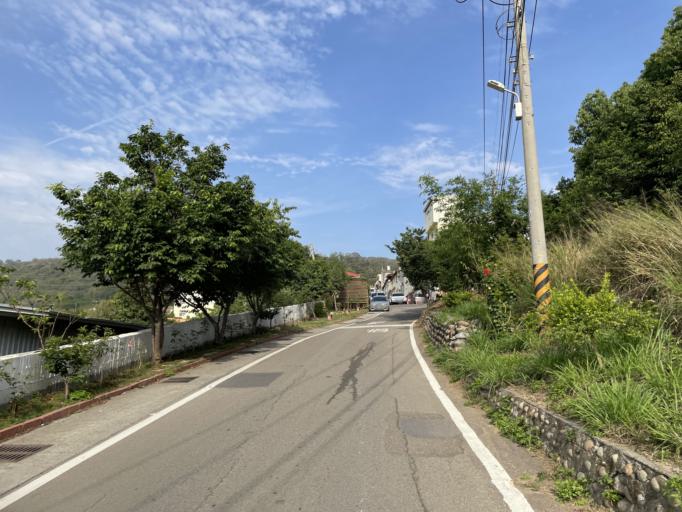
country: TW
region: Taiwan
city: Fengyuan
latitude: 24.2163
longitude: 120.7281
